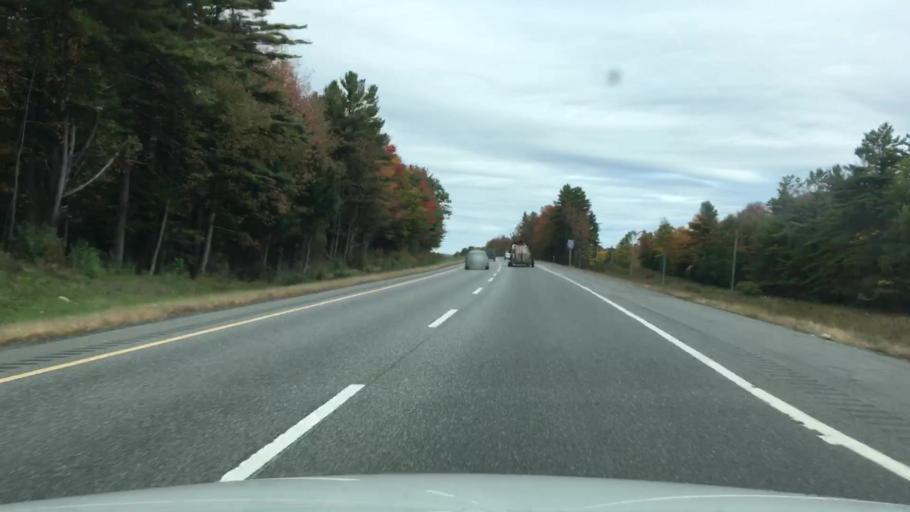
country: US
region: Maine
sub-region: Kennebec County
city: Vassalboro
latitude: 44.4568
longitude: -69.7134
